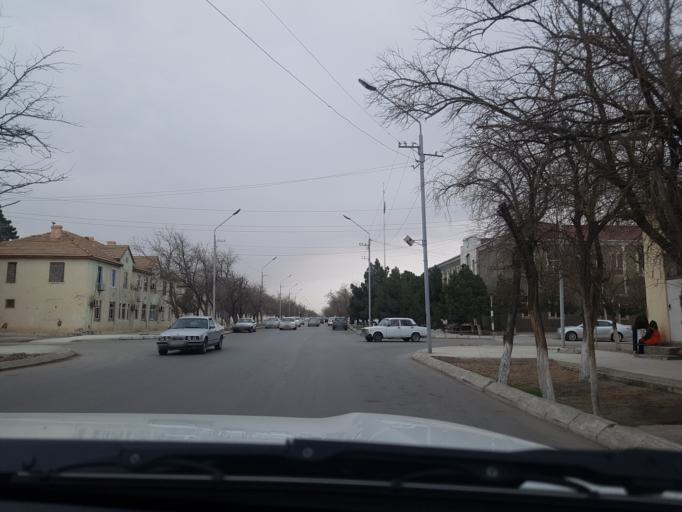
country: TM
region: Balkan
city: Balkanabat
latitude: 39.5061
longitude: 54.3590
